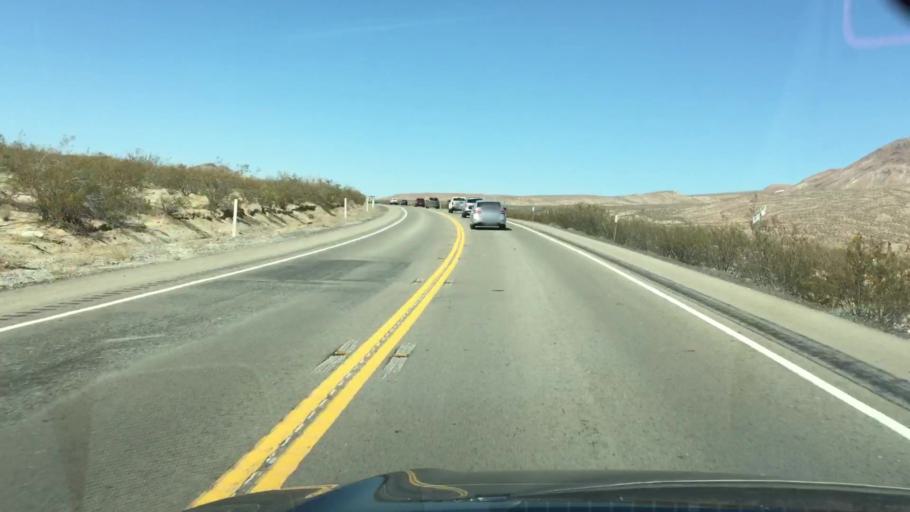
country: US
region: California
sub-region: Kern County
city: Ridgecrest
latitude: 35.3171
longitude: -117.6085
